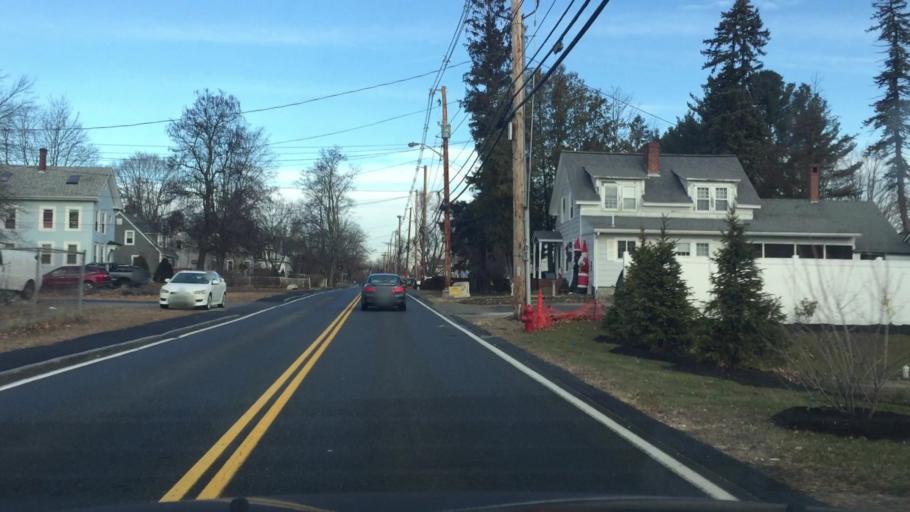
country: US
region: New Hampshire
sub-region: Rockingham County
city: Salem
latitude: 42.7786
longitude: -71.2312
